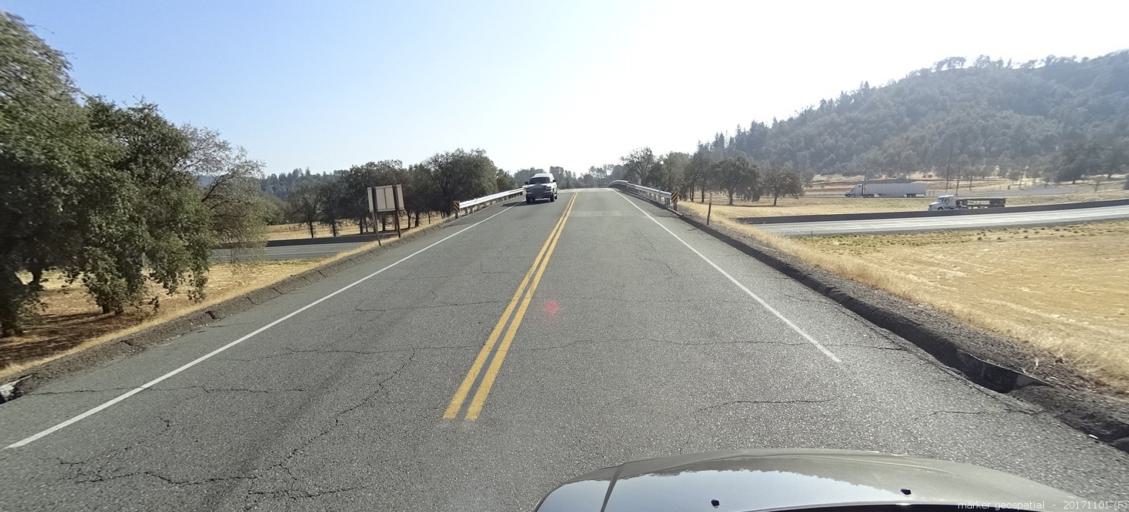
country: US
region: California
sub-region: Shasta County
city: Shasta Lake
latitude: 40.7061
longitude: -122.3381
